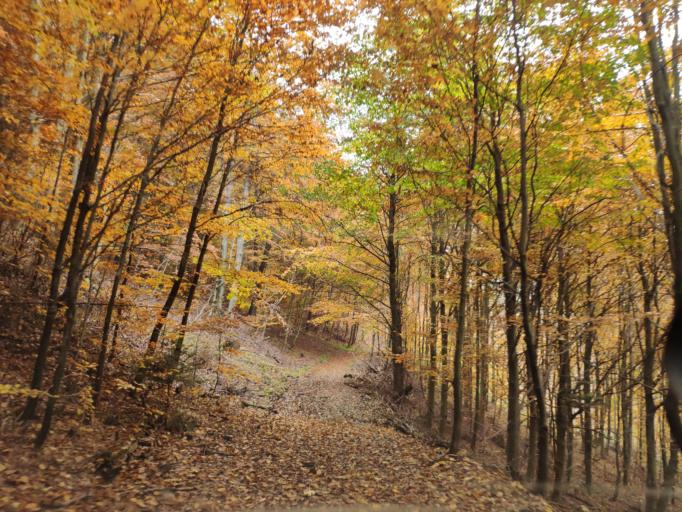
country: SK
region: Kosicky
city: Moldava nad Bodvou
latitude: 48.7400
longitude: 21.0196
